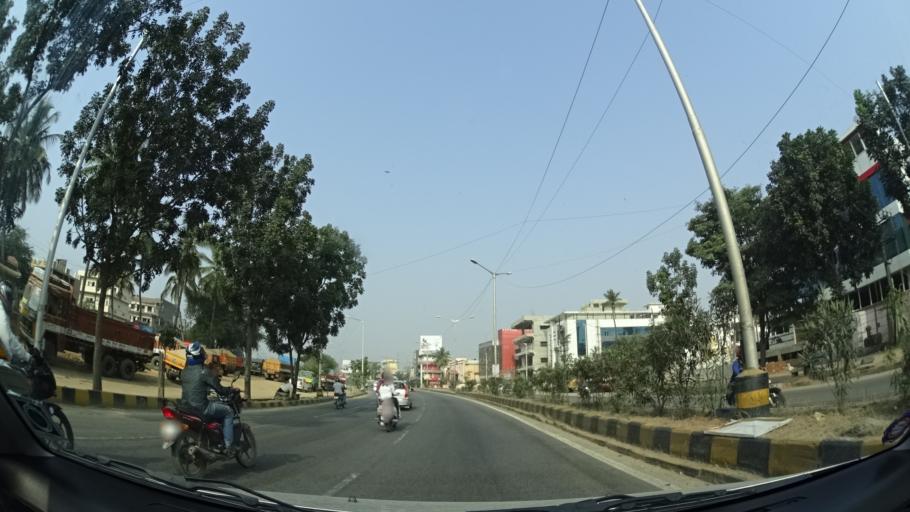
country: IN
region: Karnataka
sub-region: Bangalore Urban
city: Yelahanka
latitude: 13.0469
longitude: 77.5803
